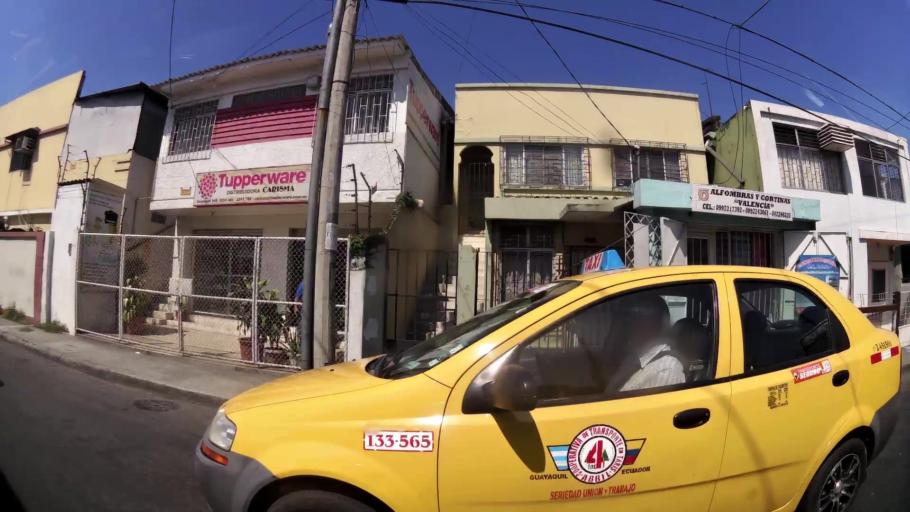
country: EC
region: Guayas
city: Guayaquil
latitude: -2.1843
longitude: -79.8932
